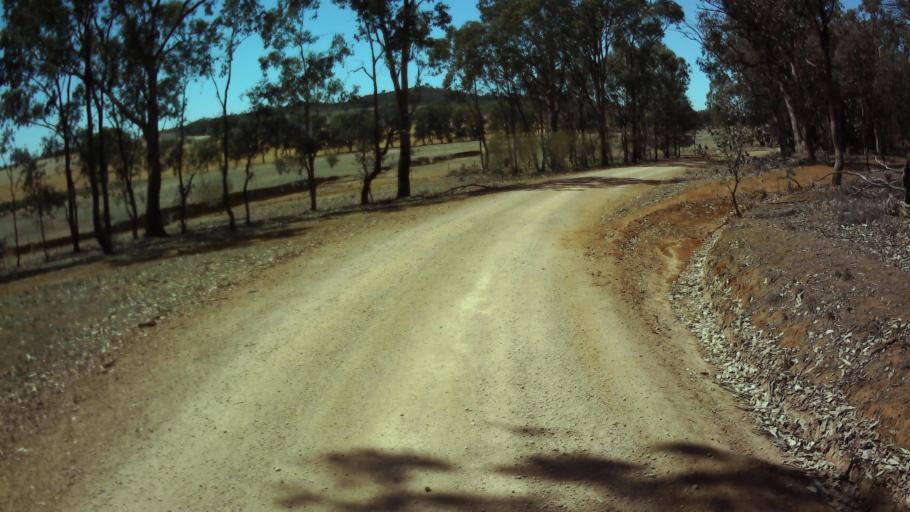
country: AU
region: New South Wales
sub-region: Weddin
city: Grenfell
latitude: -33.9482
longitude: 148.0839
